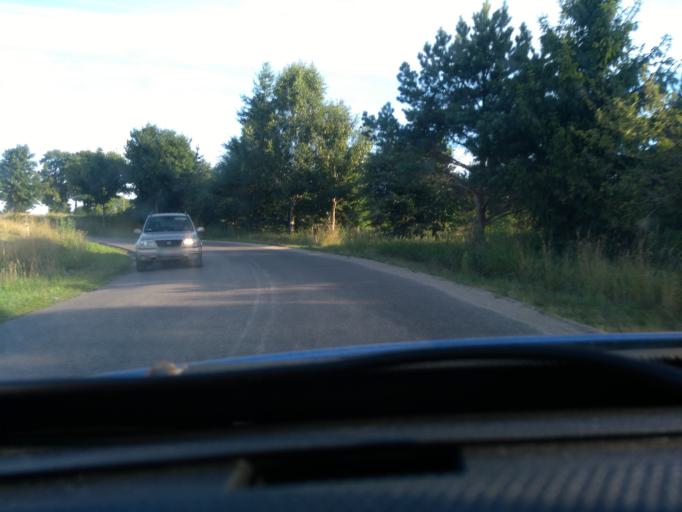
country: PL
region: Pomeranian Voivodeship
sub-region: Powiat kartuski
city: Przodkowo
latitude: 54.3952
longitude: 18.3412
